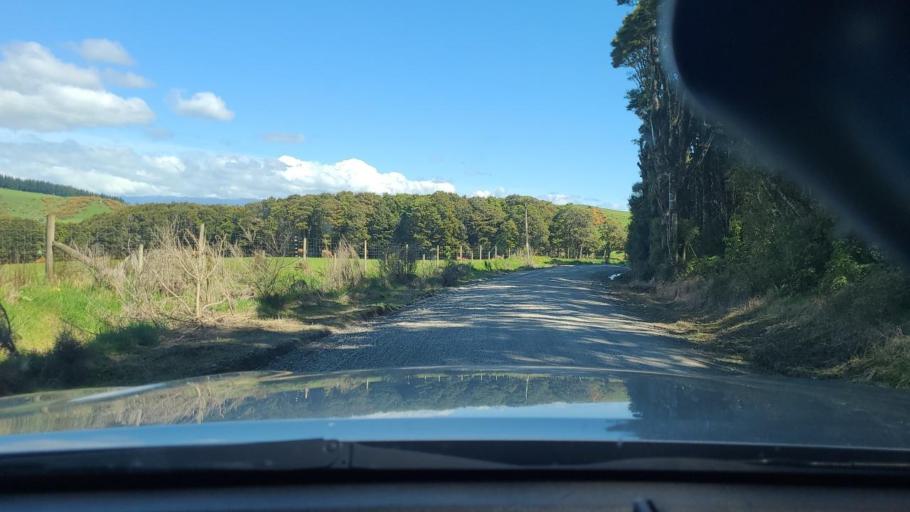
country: NZ
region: Southland
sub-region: Southland District
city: Riverton
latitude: -46.1045
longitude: 167.6222
